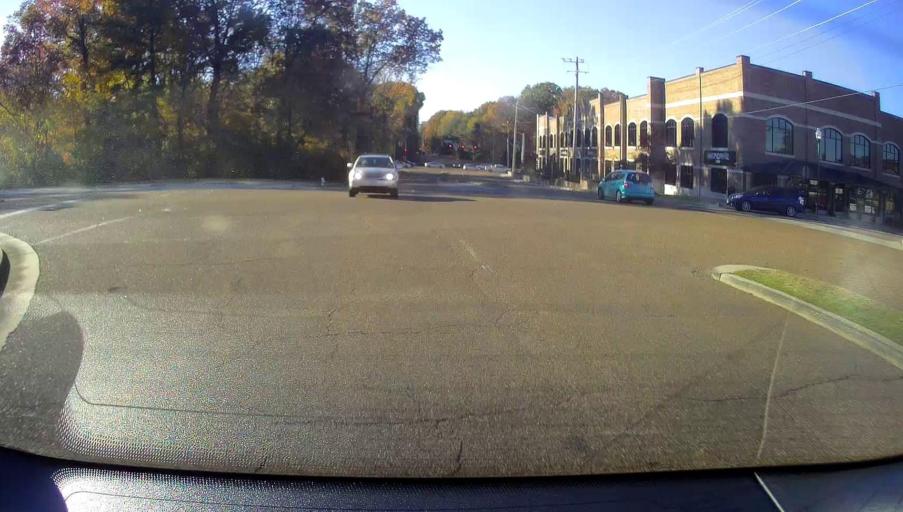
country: US
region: Tennessee
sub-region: Shelby County
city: Germantown
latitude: 35.1013
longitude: -89.8036
